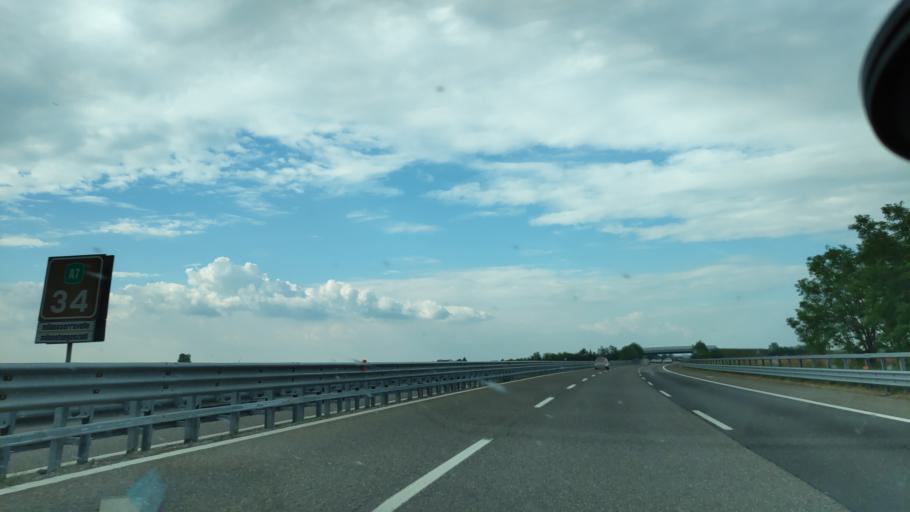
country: IT
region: Lombardy
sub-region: Provincia di Pavia
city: Pieve Albignola
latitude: 45.1267
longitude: 8.9786
